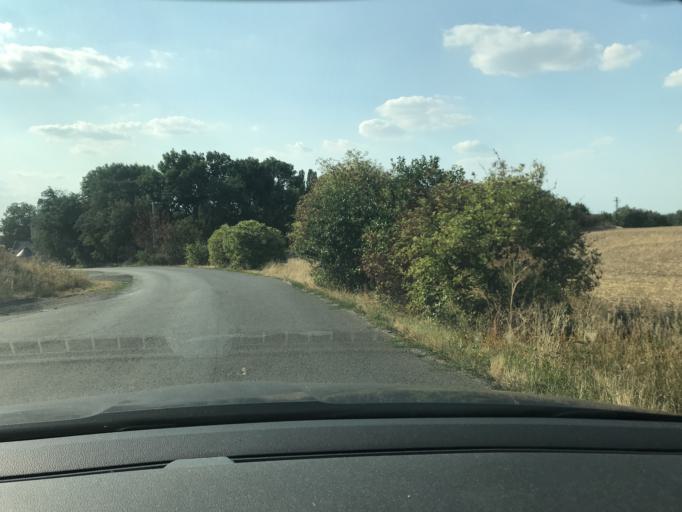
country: CZ
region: Central Bohemia
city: Kralupy nad Vltavou
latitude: 50.2323
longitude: 14.3141
